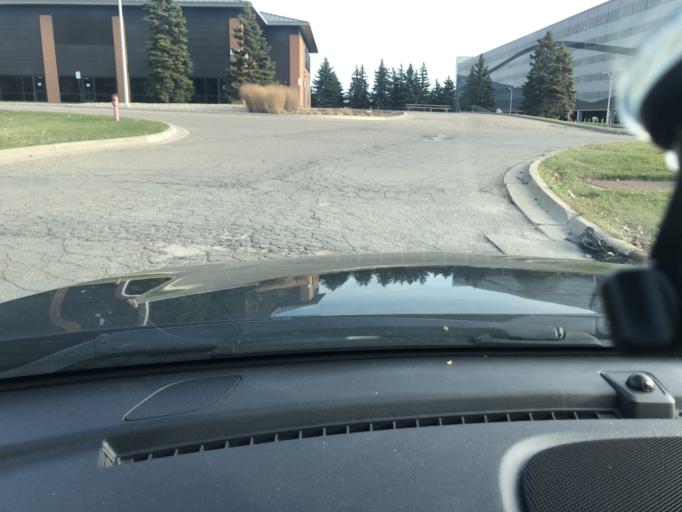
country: US
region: Michigan
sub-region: Wayne County
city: Allen Park
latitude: 42.2962
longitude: -83.2371
